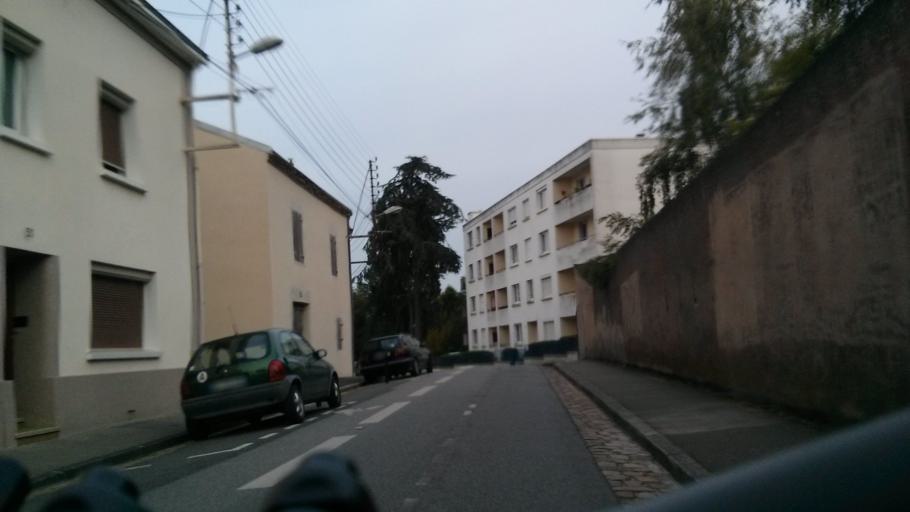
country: FR
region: Pays de la Loire
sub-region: Departement de la Loire-Atlantique
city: Reze
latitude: 47.1926
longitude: -1.5360
